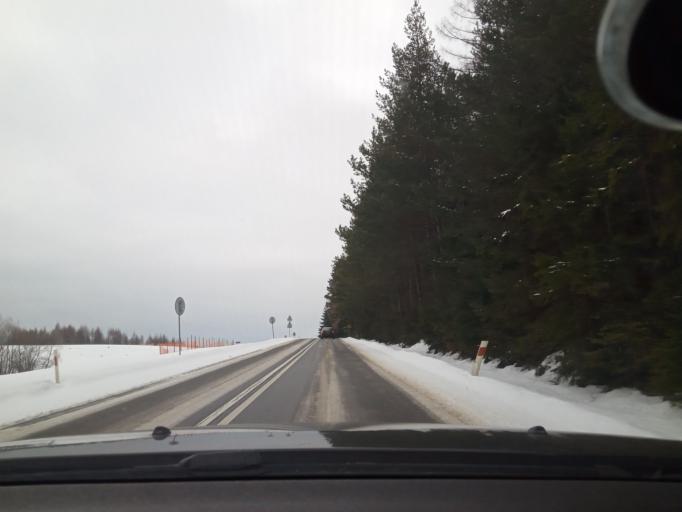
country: PL
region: Lesser Poland Voivodeship
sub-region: Powiat nowotarski
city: Krosnica
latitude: 49.4269
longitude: 20.3494
